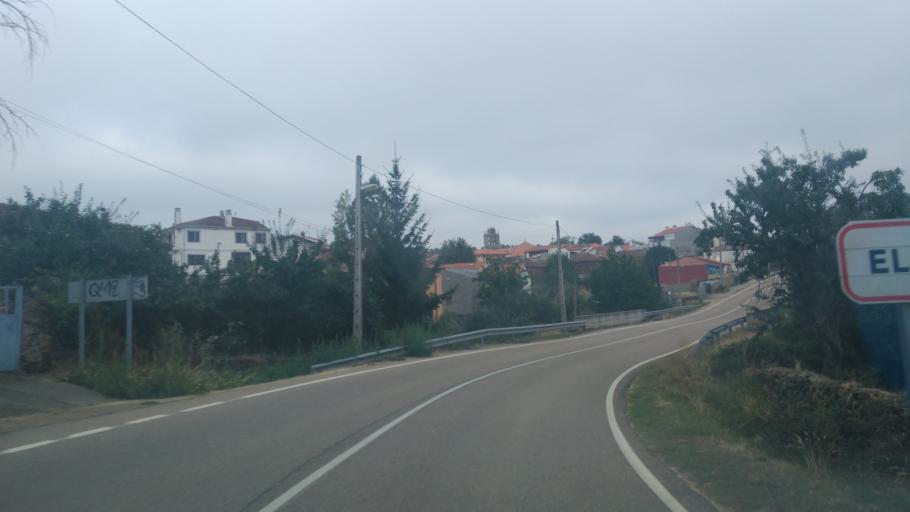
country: ES
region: Castille and Leon
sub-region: Provincia de Salamanca
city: Nava de Francia
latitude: 40.5652
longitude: -6.1242
